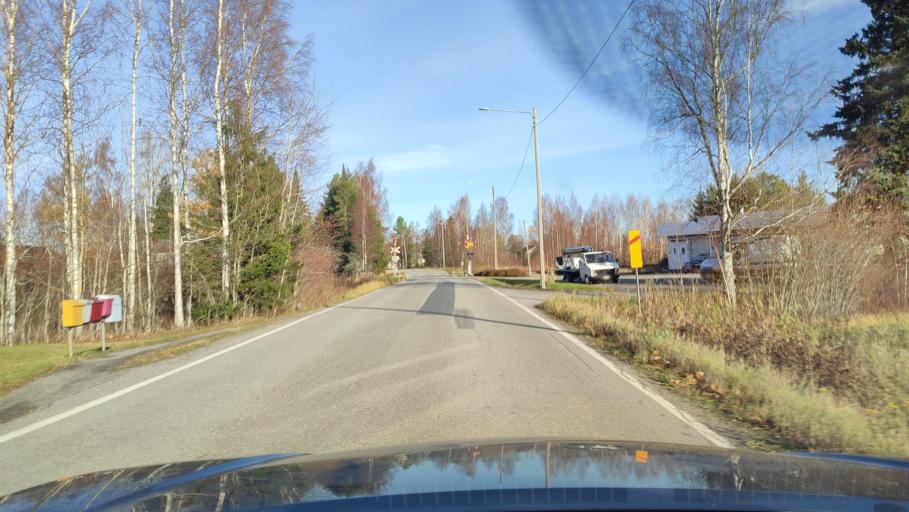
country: FI
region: Southern Ostrobothnia
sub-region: Suupohja
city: Teuva
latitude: 62.4548
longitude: 21.6046
